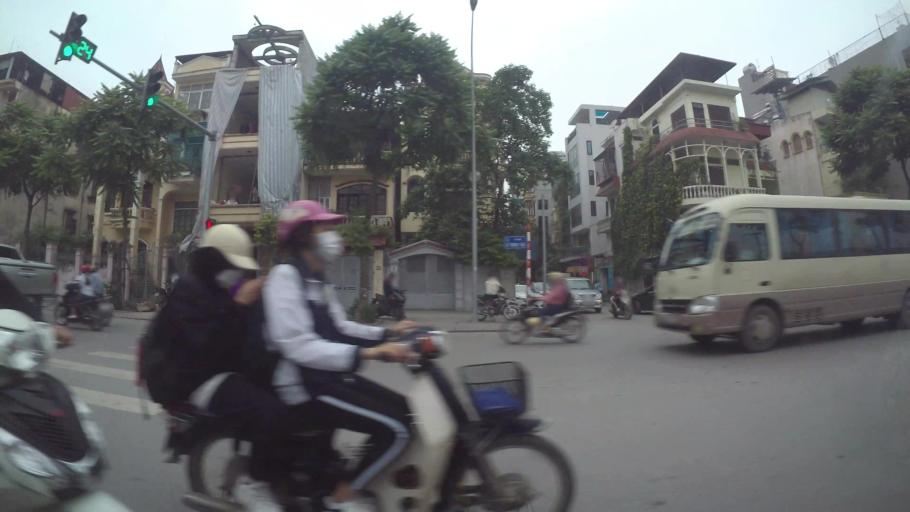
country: VN
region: Ha Noi
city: Hai BaTrung
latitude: 20.9916
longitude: 105.8327
